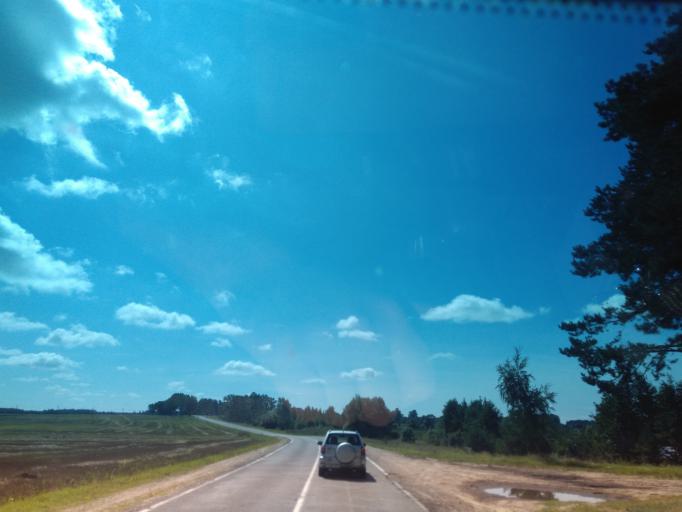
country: BY
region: Minsk
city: Uzda
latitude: 53.2945
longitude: 27.2389
